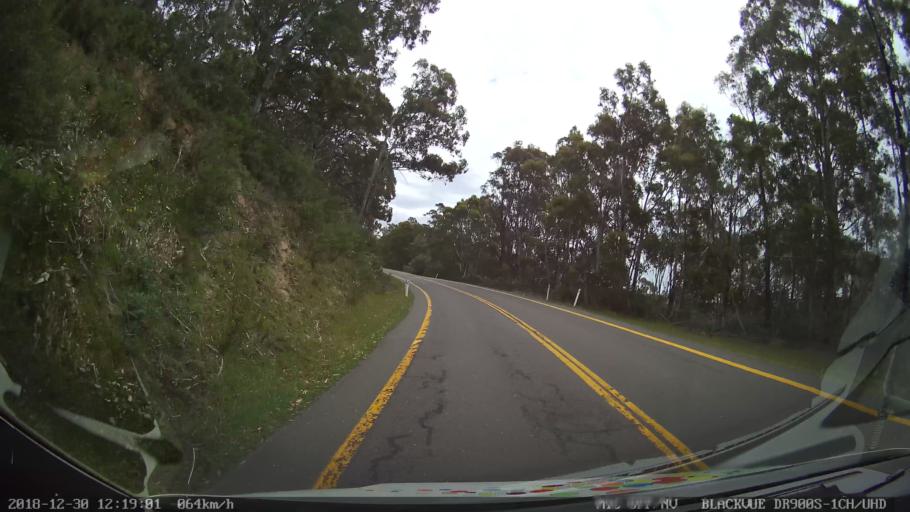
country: AU
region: New South Wales
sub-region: Snowy River
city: Jindabyne
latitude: -36.3490
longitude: 148.5448
